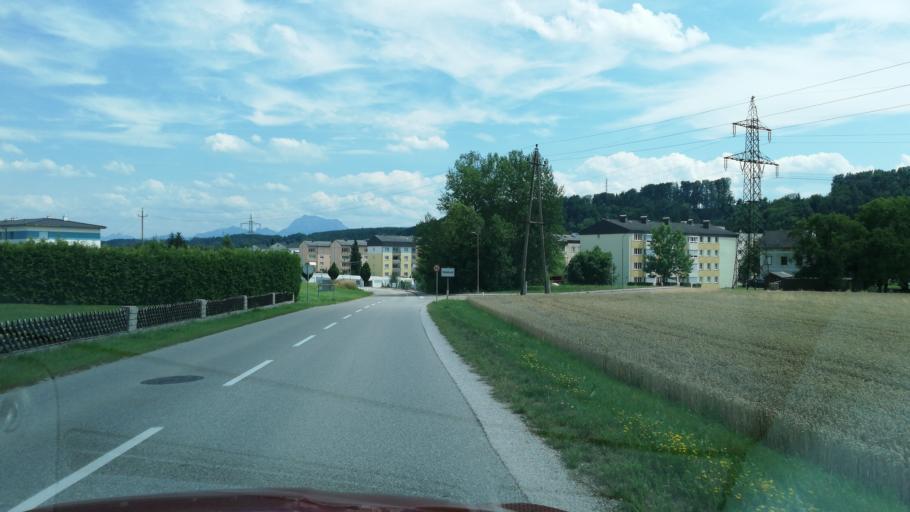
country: AT
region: Upper Austria
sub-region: Politischer Bezirk Vocklabruck
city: Vocklabruck
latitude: 47.9984
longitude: 13.6355
